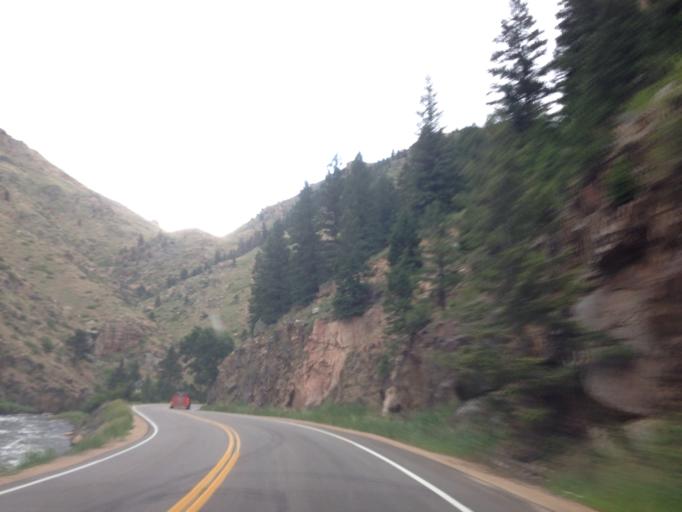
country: US
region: Colorado
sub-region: Larimer County
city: Laporte
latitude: 40.6930
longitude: -105.3779
